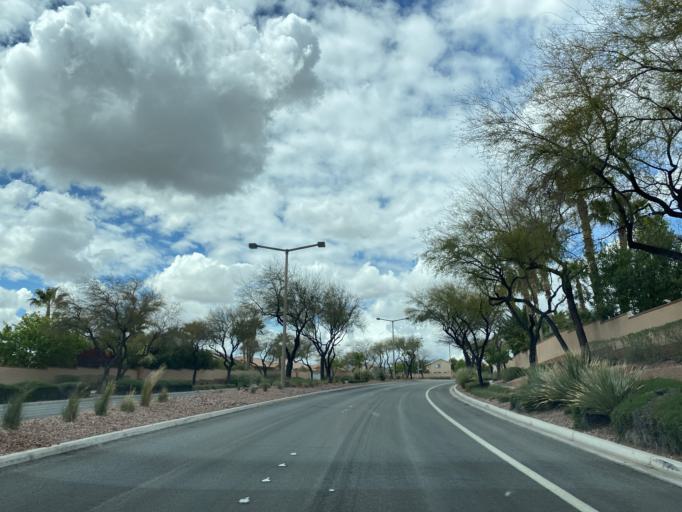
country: US
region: Nevada
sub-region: Clark County
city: Summerlin South
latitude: 36.1801
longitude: -115.3317
